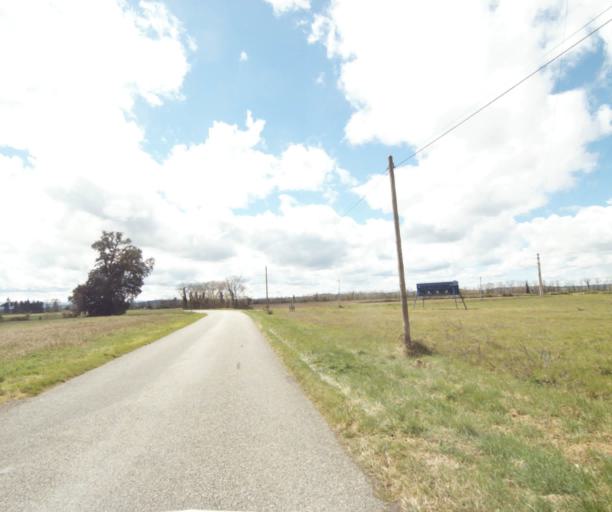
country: FR
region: Midi-Pyrenees
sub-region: Departement de l'Ariege
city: Saverdun
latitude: 43.2559
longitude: 1.6005
